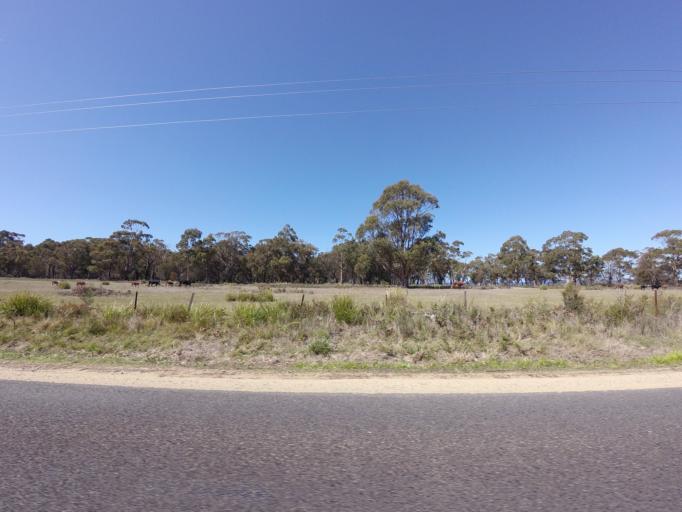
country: AU
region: Tasmania
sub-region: Break O'Day
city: St Helens
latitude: -41.6969
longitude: 148.2779
